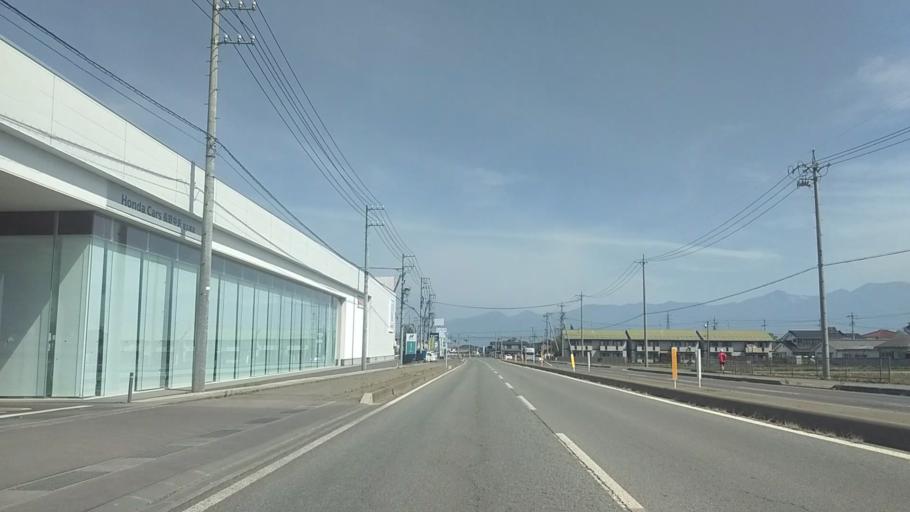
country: JP
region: Nagano
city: Saku
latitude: 36.2095
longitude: 138.4659
